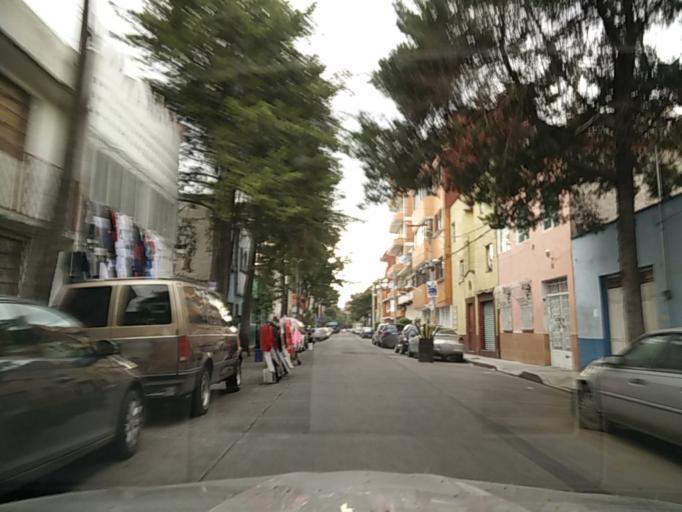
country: MX
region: Mexico City
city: Mexico City
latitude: 19.4112
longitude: -99.1400
